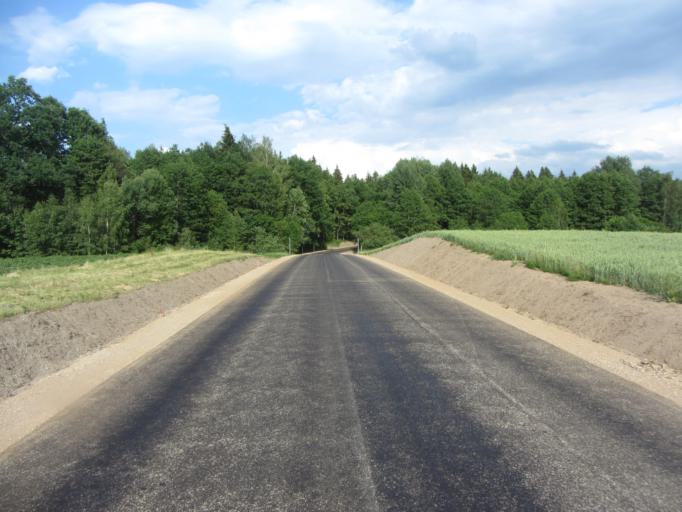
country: LT
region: Alytaus apskritis
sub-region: Alytaus rajonas
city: Daugai
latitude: 54.4626
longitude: 24.3514
